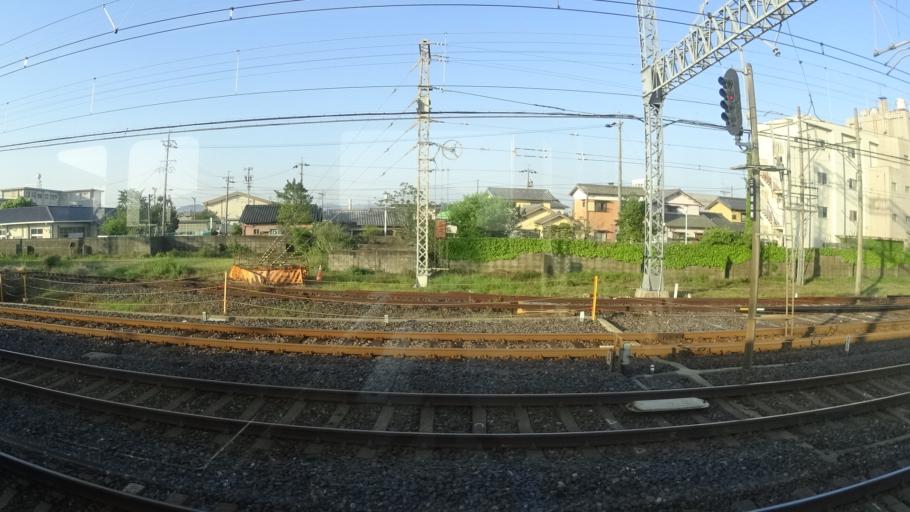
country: JP
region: Mie
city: Ise
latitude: 34.5492
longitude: 136.5821
